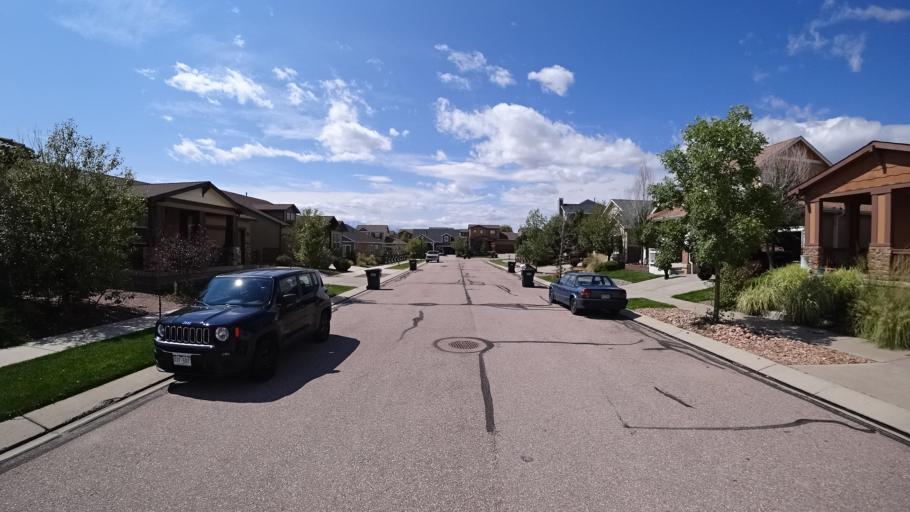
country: US
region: Colorado
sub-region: El Paso County
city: Cimarron Hills
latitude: 38.9307
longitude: -104.6794
